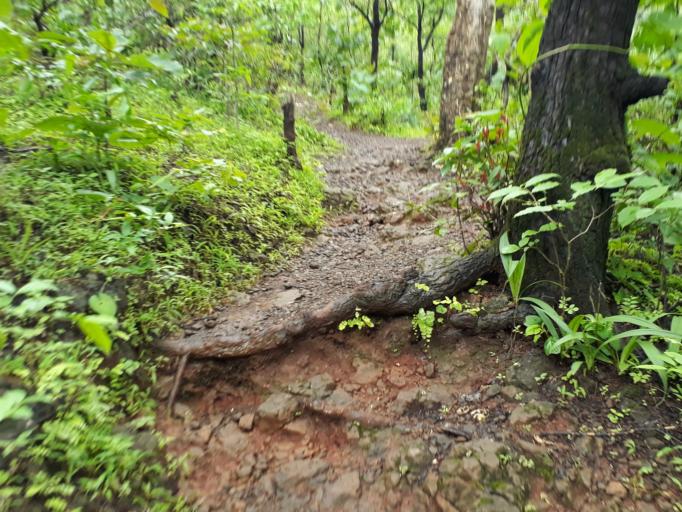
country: IN
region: Maharashtra
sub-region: Raigarh
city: Khopoli
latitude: 18.8403
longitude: 73.3827
